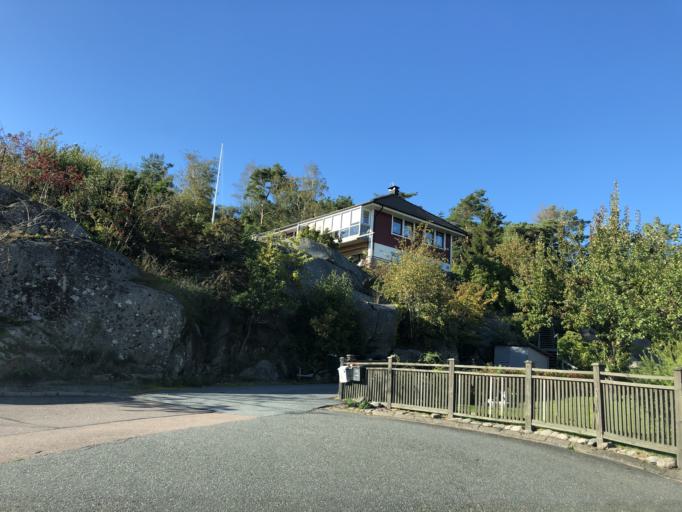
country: SE
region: Vaestra Goetaland
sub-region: Goteborg
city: Majorna
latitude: 57.6538
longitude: 11.8606
